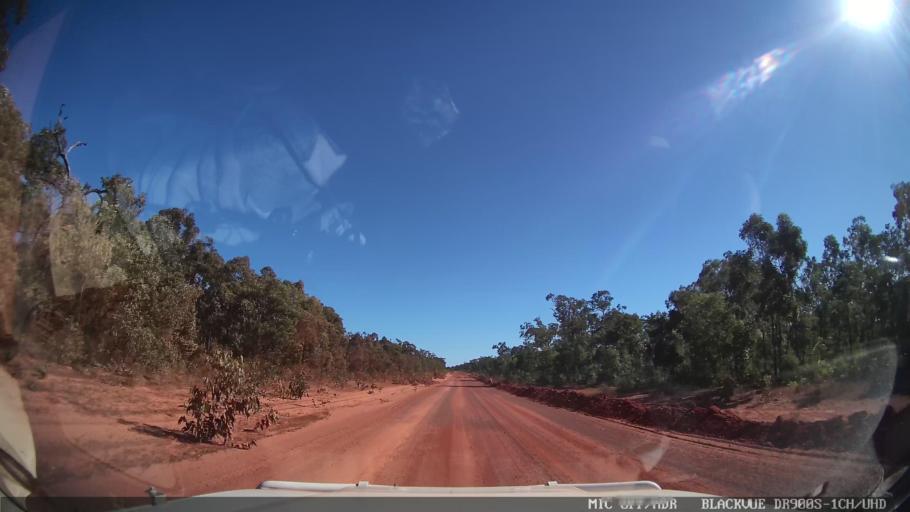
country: AU
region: Queensland
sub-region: Torres
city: Thursday Island
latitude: -11.3925
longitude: 142.3559
